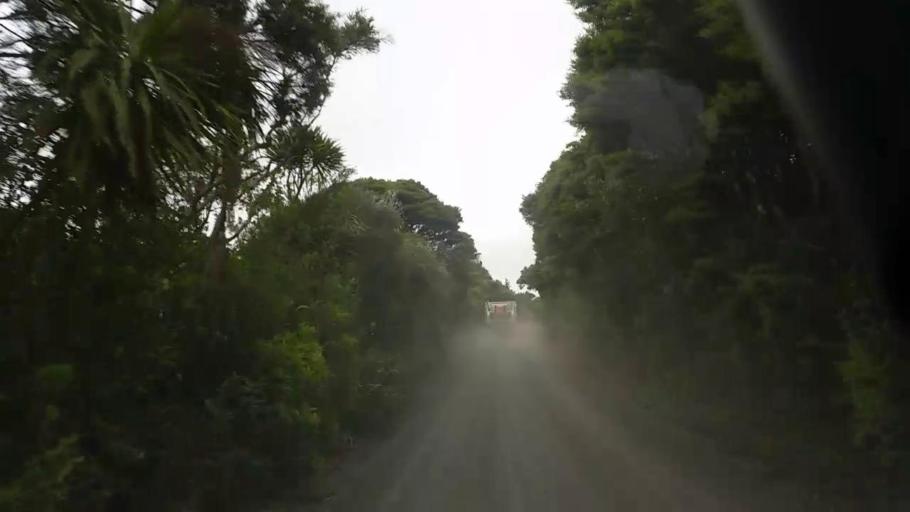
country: NZ
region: Auckland
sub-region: Auckland
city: Muriwai Beach
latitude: -36.9260
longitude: 174.4887
